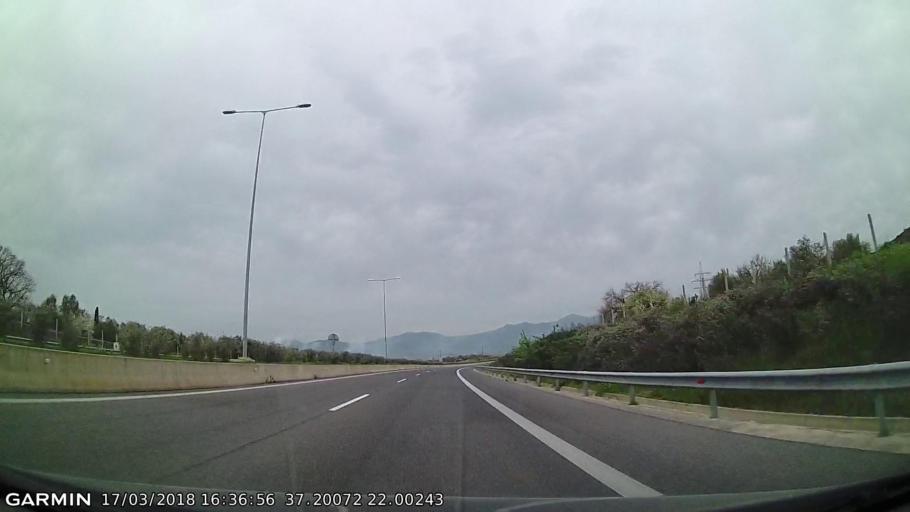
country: GR
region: Peloponnese
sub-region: Nomos Messinias
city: Meligalas
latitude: 37.2014
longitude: 22.0020
